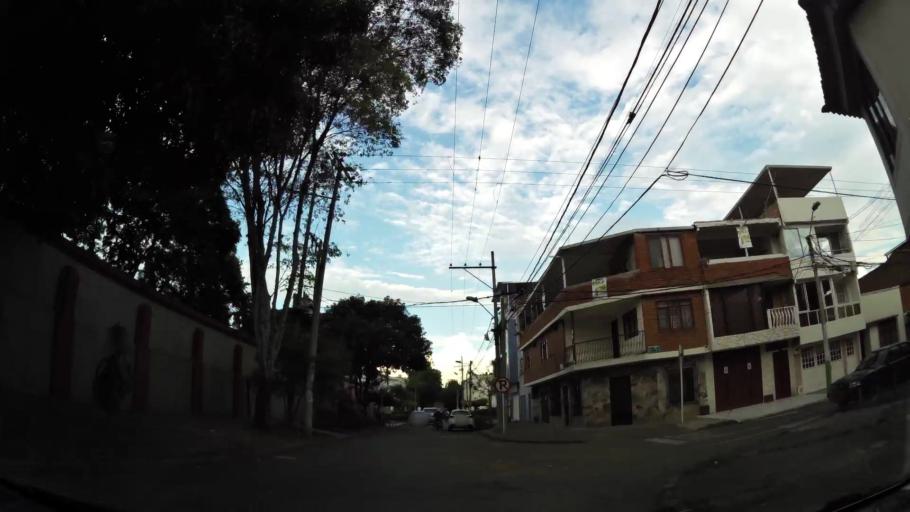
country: CO
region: Valle del Cauca
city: Cali
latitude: 3.4601
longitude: -76.5179
